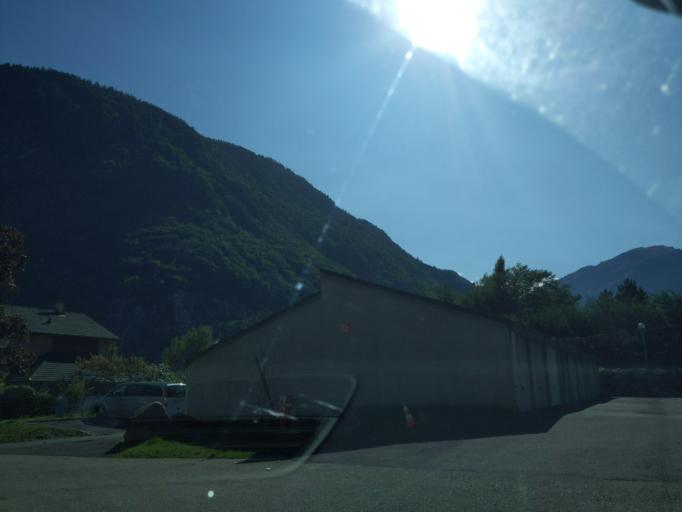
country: FR
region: Rhone-Alpes
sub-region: Departement de la Savoie
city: Saint-Jean-de-Maurienne
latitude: 45.2700
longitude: 6.3421
